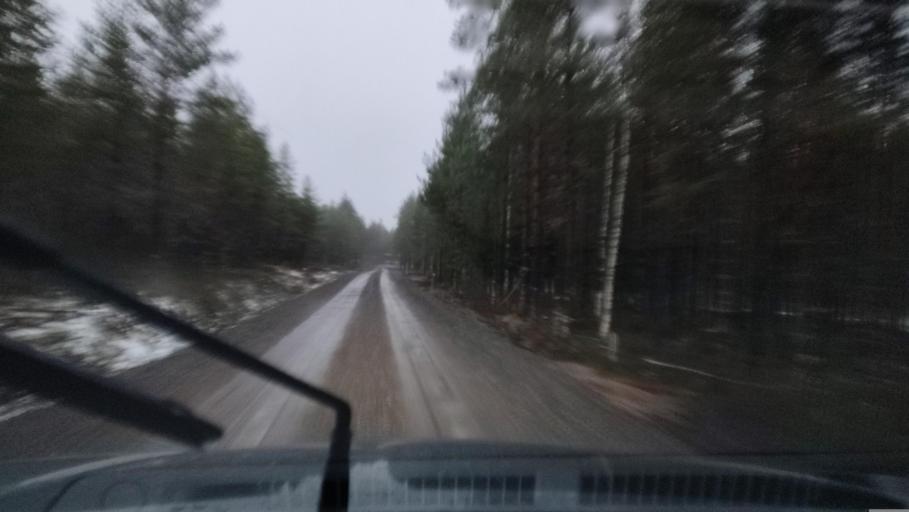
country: FI
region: Southern Ostrobothnia
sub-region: Suupohja
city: Karijoki
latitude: 62.1485
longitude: 21.6237
